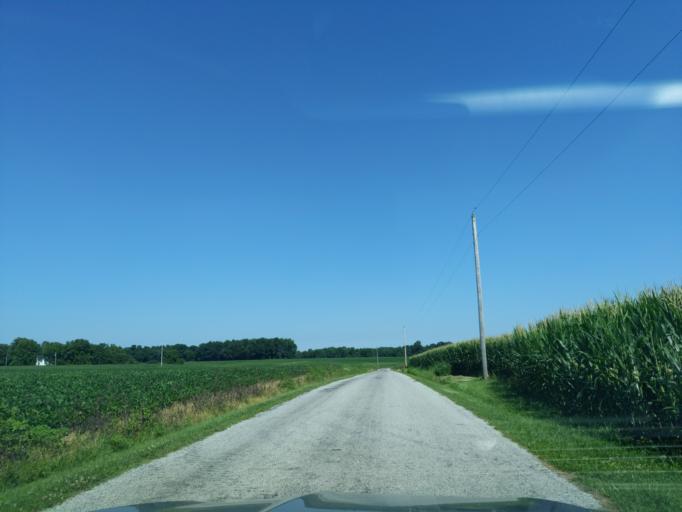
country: US
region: Indiana
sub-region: Ripley County
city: Osgood
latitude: 39.0804
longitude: -85.4316
